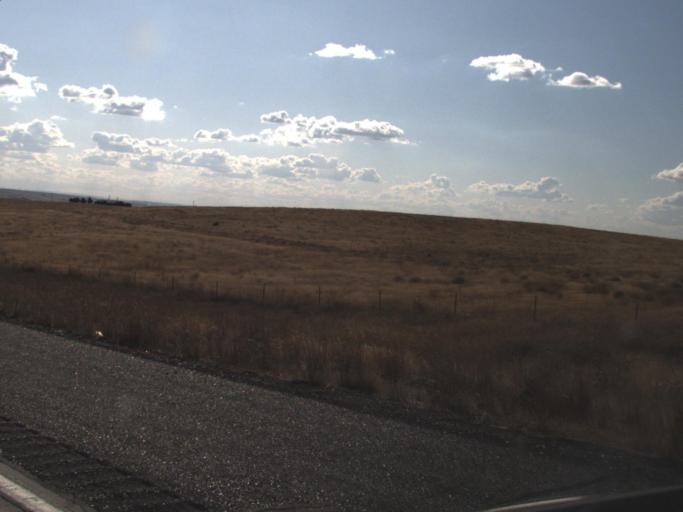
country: US
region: Oregon
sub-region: Umatilla County
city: Umatilla
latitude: 45.9661
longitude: -119.3421
